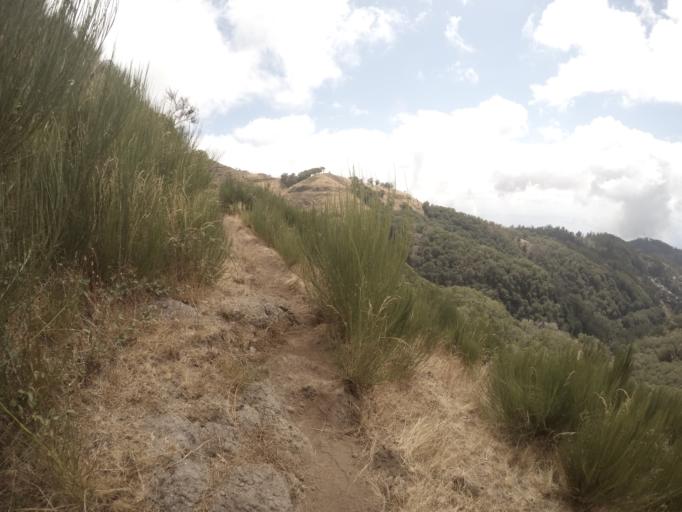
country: PT
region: Madeira
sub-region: Camara de Lobos
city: Curral das Freiras
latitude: 32.7096
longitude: -17.0070
